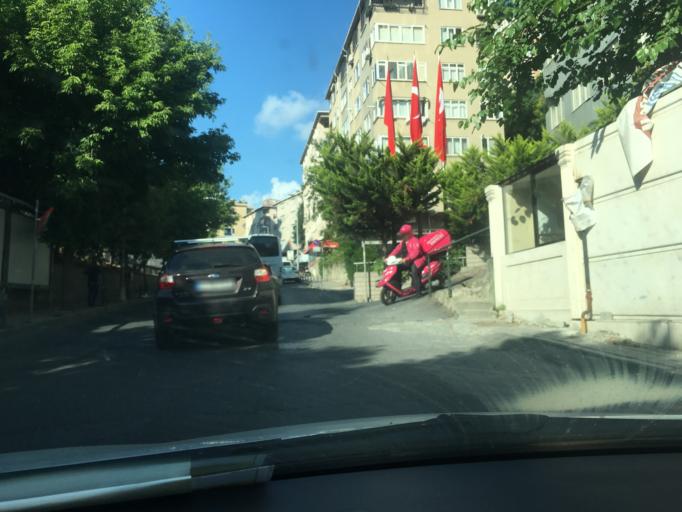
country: TR
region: Istanbul
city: Sisli
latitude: 41.0584
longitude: 29.0038
